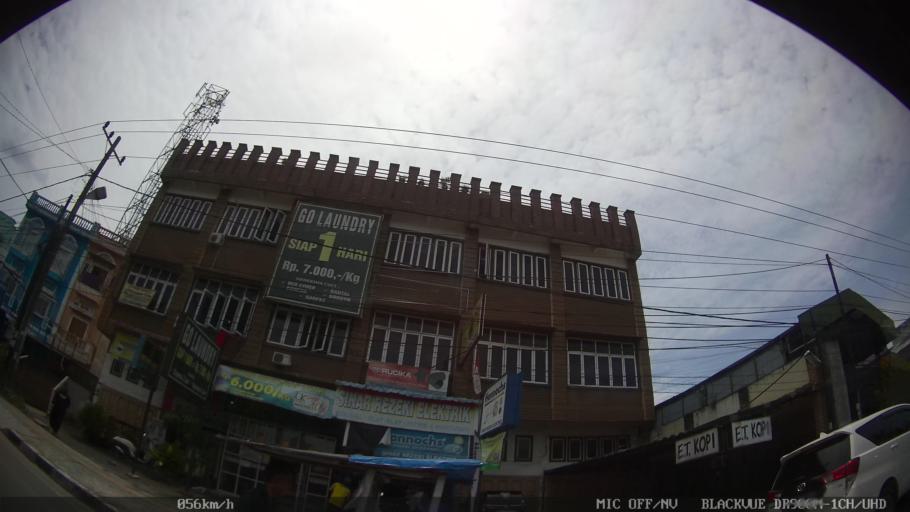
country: ID
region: North Sumatra
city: Sunggal
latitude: 3.5481
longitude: 98.6277
